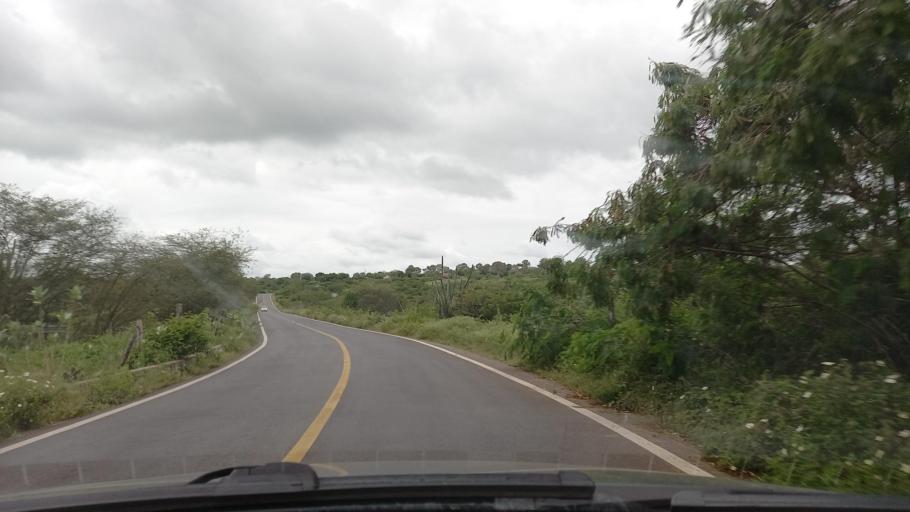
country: BR
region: Sergipe
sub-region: Caninde De Sao Francisco
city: Caninde de Sao Francisco
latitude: -9.6168
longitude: -37.7730
